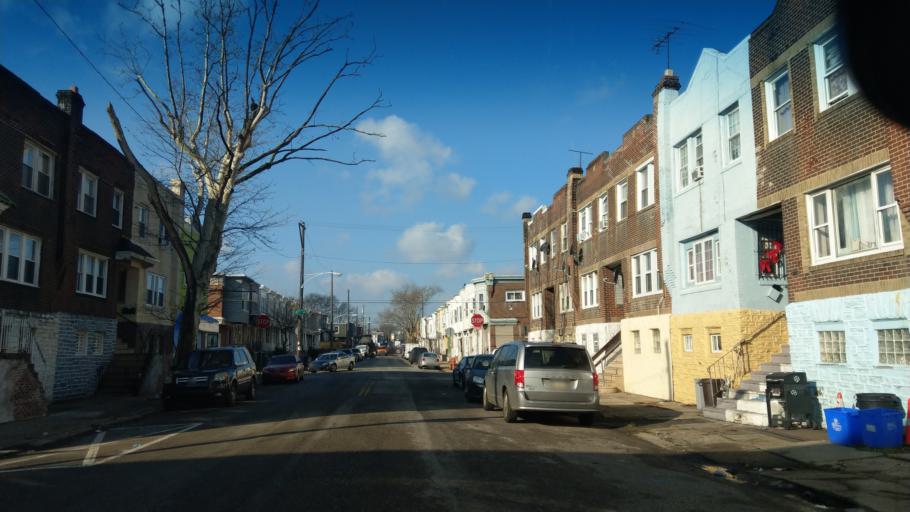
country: US
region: Pennsylvania
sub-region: Montgomery County
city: Rockledge
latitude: 40.0200
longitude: -75.1316
